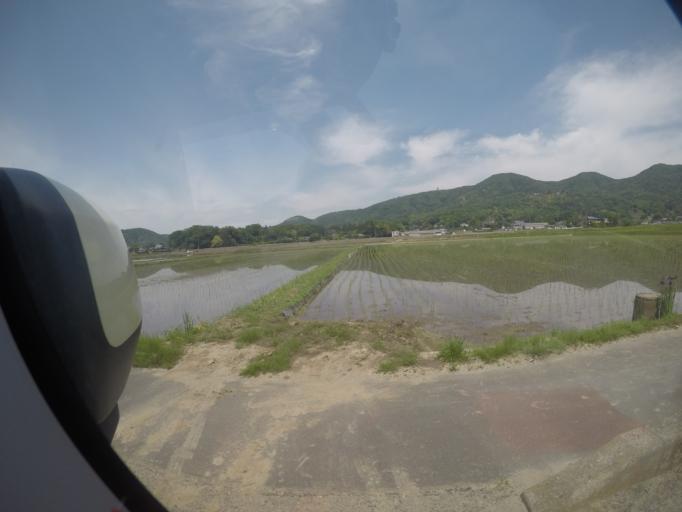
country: JP
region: Ibaraki
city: Iwase
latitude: 36.3213
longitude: 140.1101
